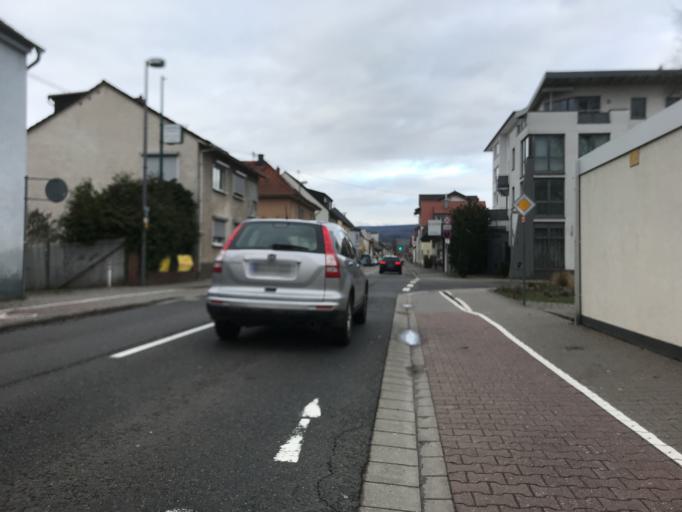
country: DE
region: Rheinland-Pfalz
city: Oestrich-Winkel
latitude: 49.9881
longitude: 8.0263
